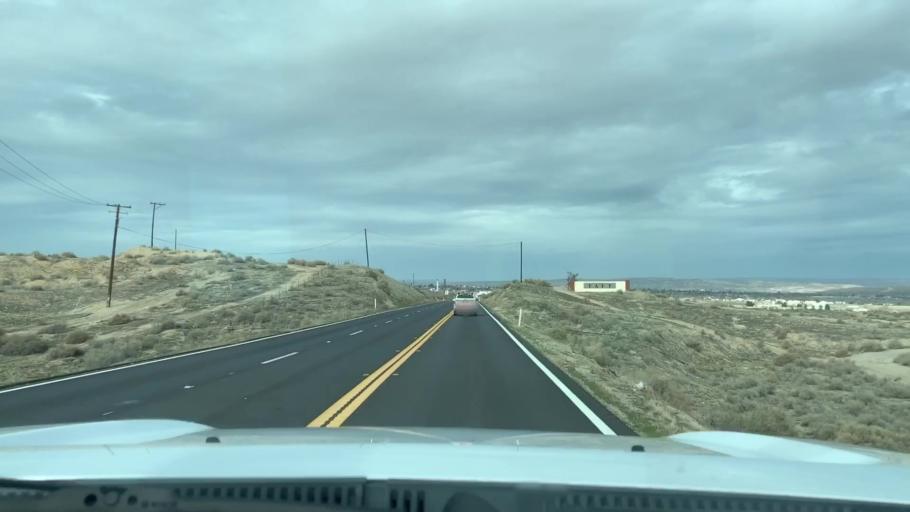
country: US
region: California
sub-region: Kern County
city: South Taft
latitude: 35.1229
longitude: -119.4370
